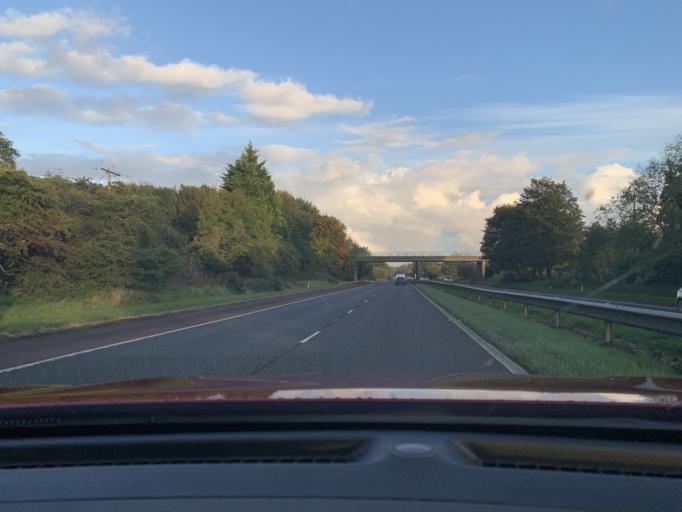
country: GB
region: Northern Ireland
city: Moira
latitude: 54.4714
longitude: -6.1644
